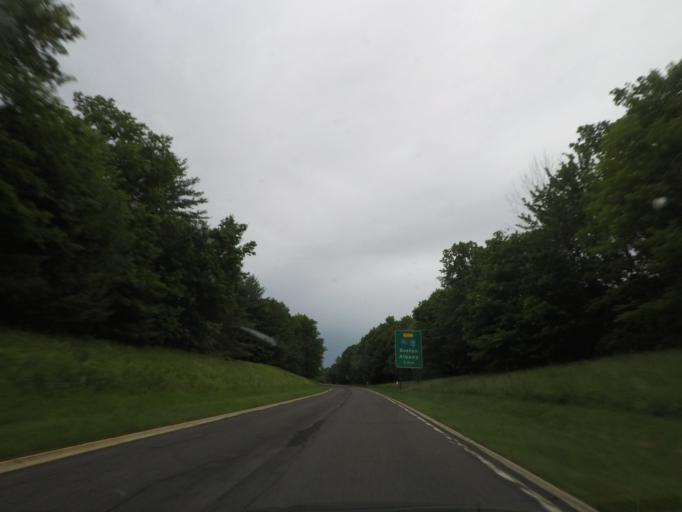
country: US
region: New York
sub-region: Columbia County
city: Chatham
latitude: 42.4022
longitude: -73.5488
